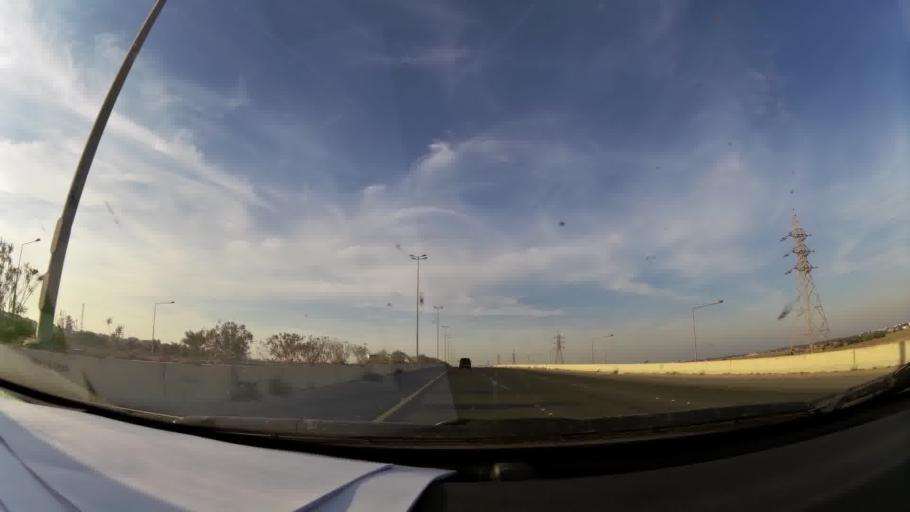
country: KW
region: Al Ahmadi
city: Al Fahahil
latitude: 28.9642
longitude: 48.1658
